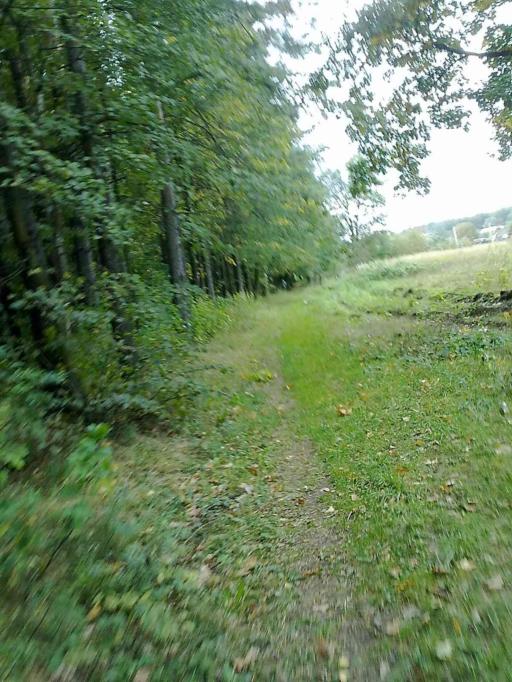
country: RU
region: Moskovskaya
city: Kokoshkino
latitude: 55.6116
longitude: 37.1900
